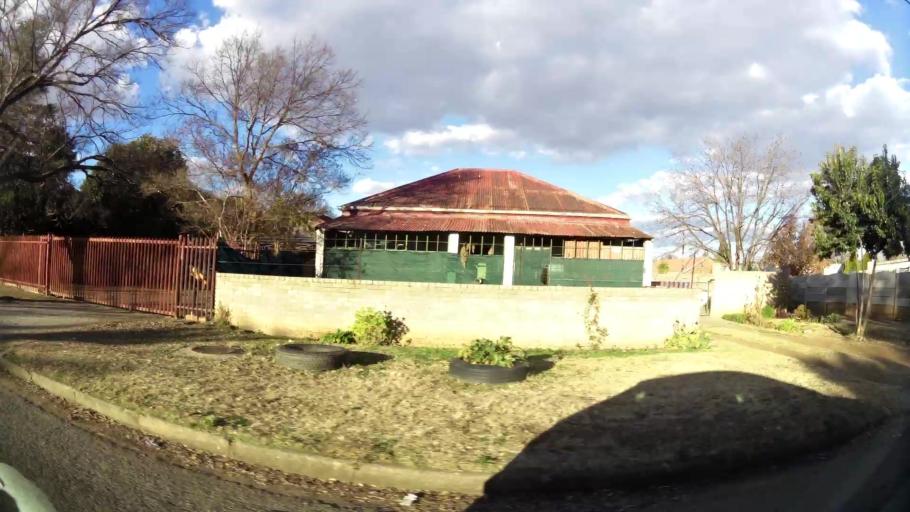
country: ZA
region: North-West
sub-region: Dr Kenneth Kaunda District Municipality
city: Potchefstroom
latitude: -26.7373
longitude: 27.0836
